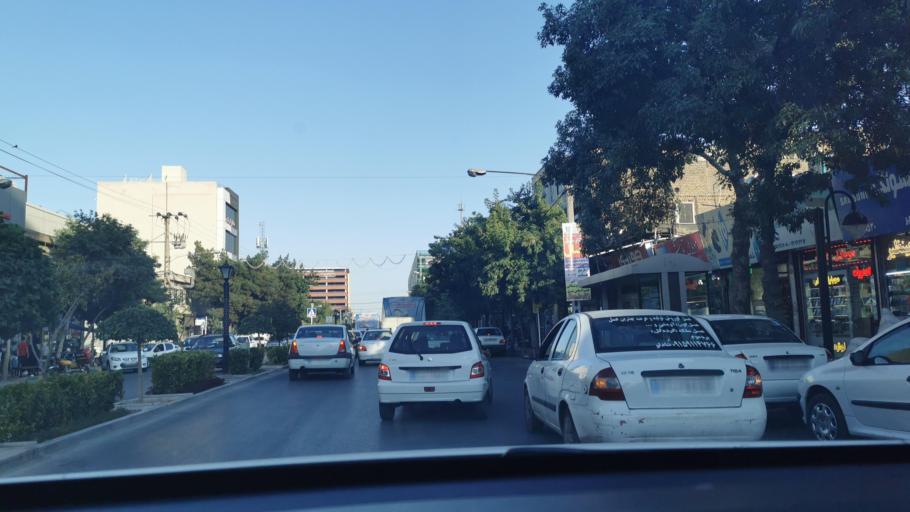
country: IR
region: Razavi Khorasan
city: Mashhad
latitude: 36.2944
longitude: 59.6450
